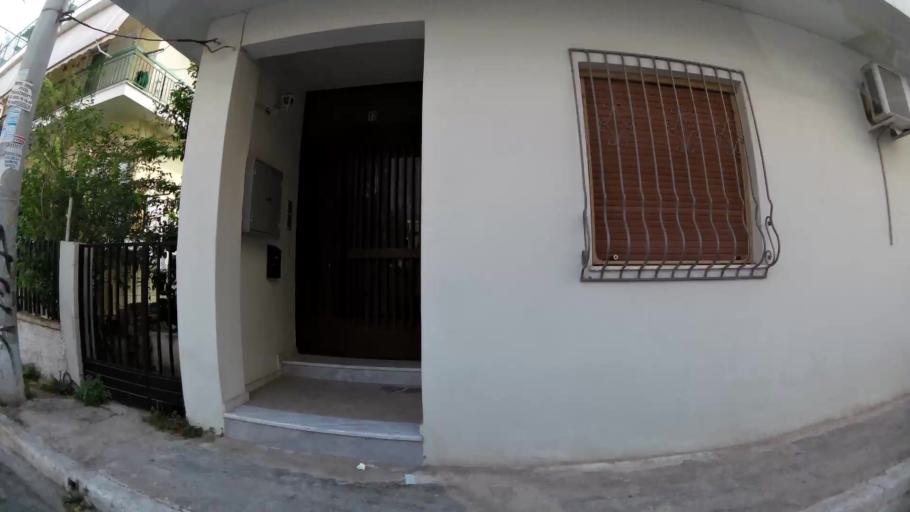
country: GR
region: Attica
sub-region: Nomarchia Athinas
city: Agios Dimitrios
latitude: 37.9358
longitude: 23.7268
